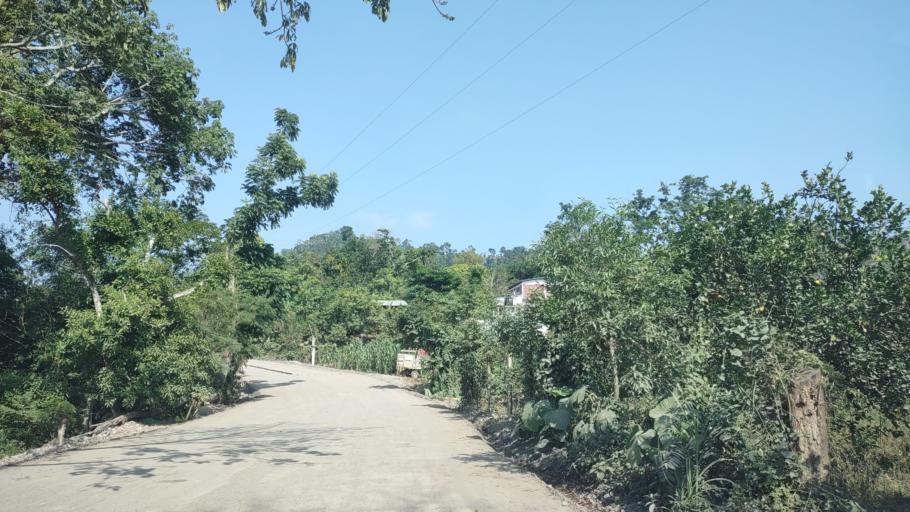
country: MX
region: Veracruz
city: Agua Dulce
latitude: 20.2934
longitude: -97.2843
